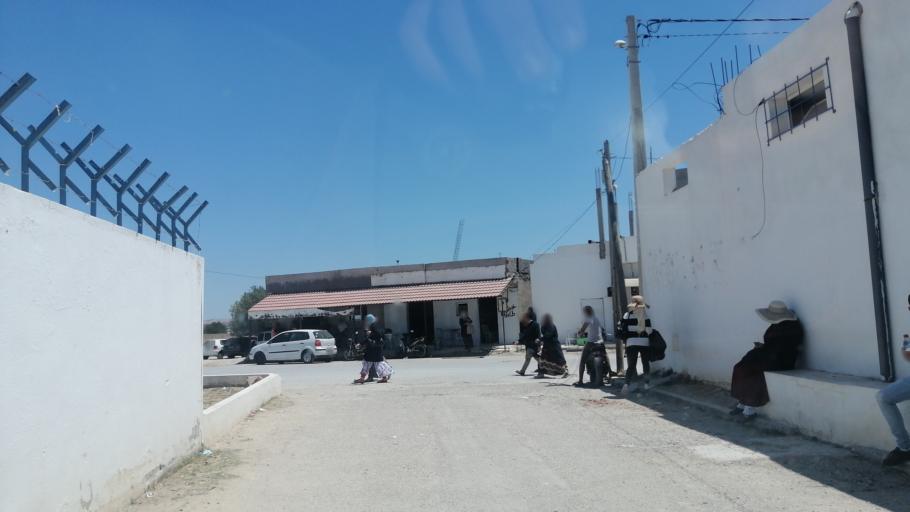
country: TN
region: Al Qayrawan
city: Sbikha
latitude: 36.1214
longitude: 10.0966
